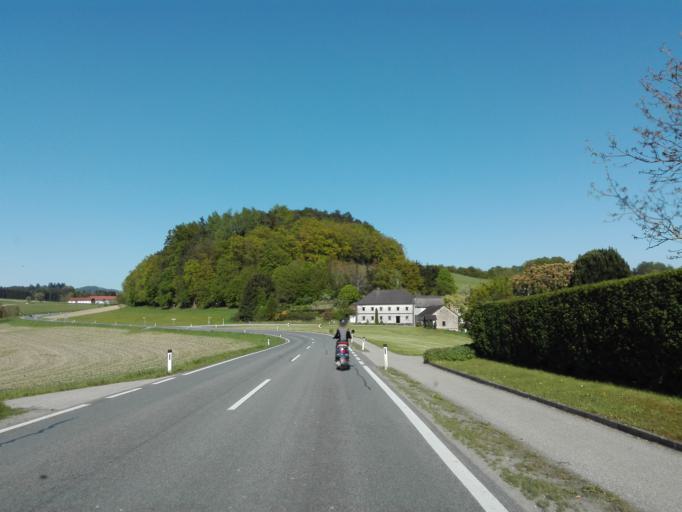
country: AT
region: Upper Austria
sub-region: Politischer Bezirk Perg
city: Perg
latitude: 48.2624
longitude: 14.6724
